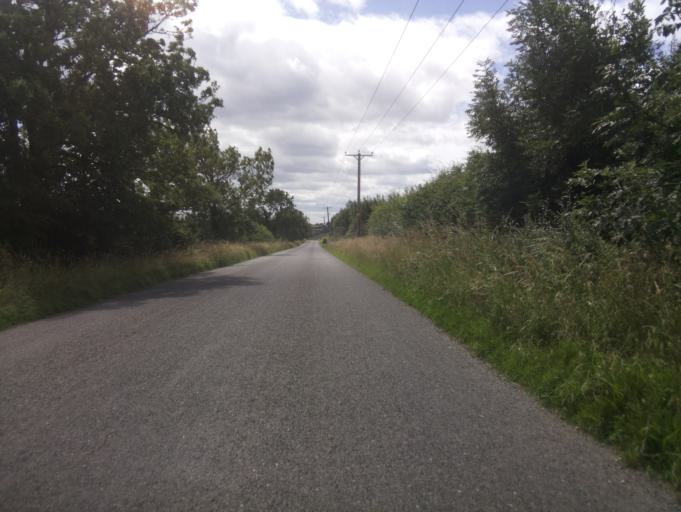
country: GB
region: England
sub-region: Nottinghamshire
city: Ruddington
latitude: 52.8659
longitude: -1.0936
